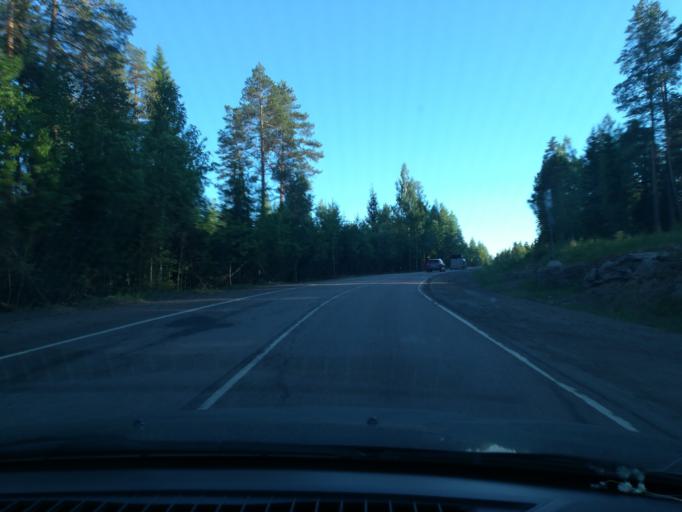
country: RU
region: Leningrad
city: Lesogorskiy
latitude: 60.9968
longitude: 28.9147
